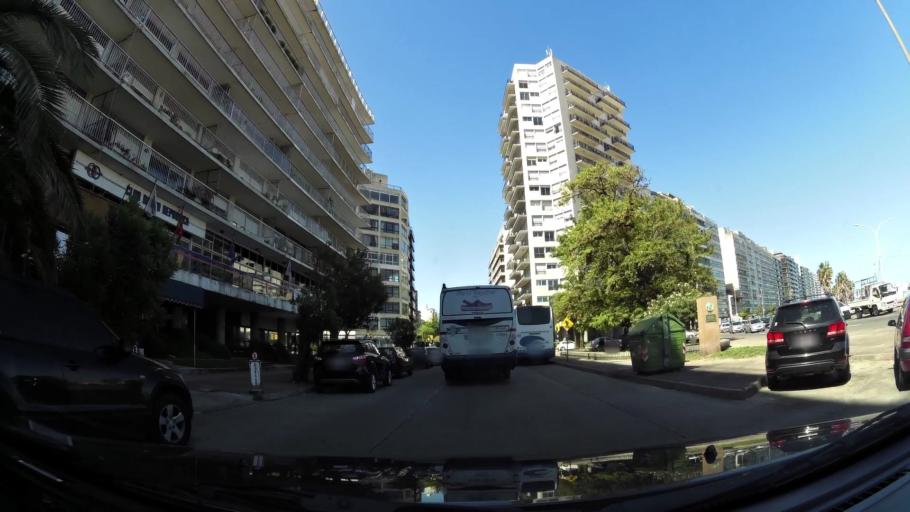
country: UY
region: Montevideo
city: Montevideo
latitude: -34.9095
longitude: -56.1435
